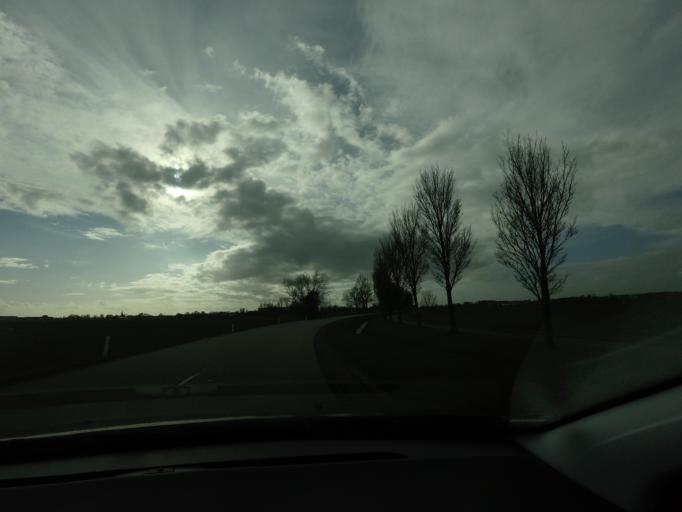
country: NL
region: Friesland
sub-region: Gemeente Boarnsterhim
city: Jirnsum
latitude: 53.0856
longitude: 5.8066
